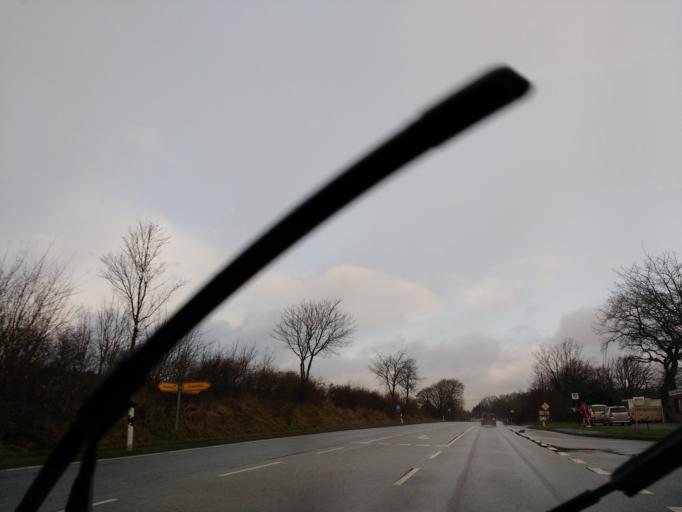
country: DE
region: Schleswig-Holstein
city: Goosefeld
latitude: 54.4322
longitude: 9.8114
